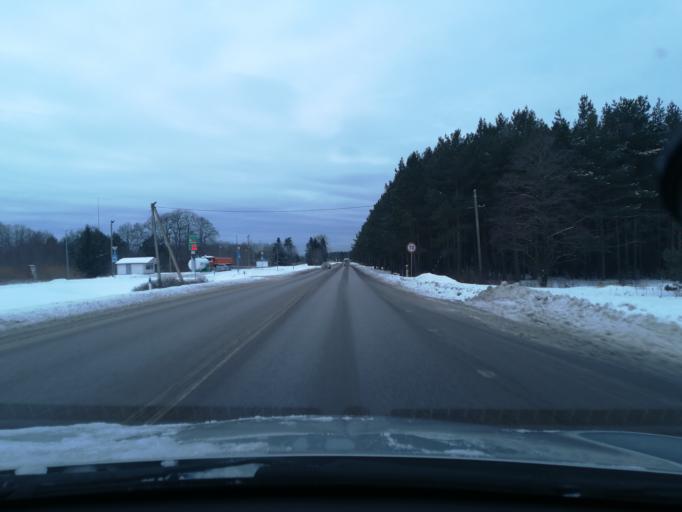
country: EE
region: Harju
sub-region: Harku vald
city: Tabasalu
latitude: 59.4339
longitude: 24.5894
